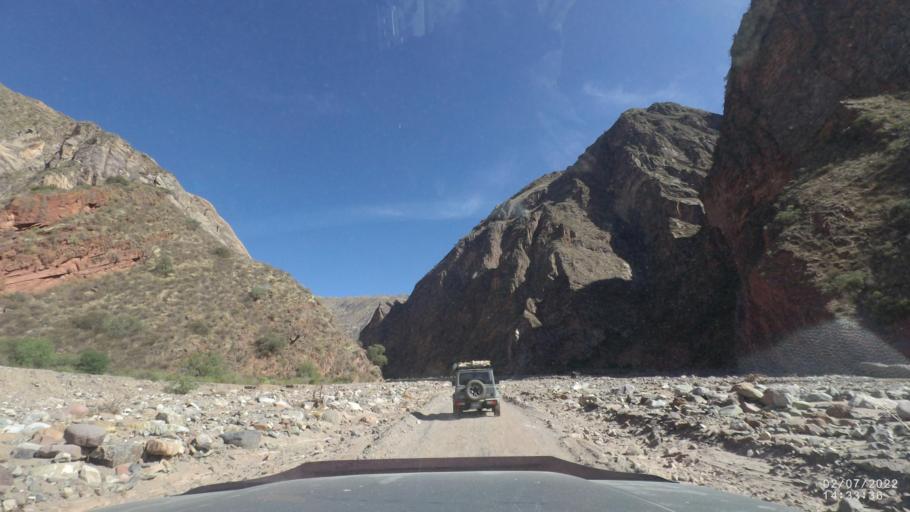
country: BO
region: Cochabamba
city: Irpa Irpa
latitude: -17.8382
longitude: -66.4158
